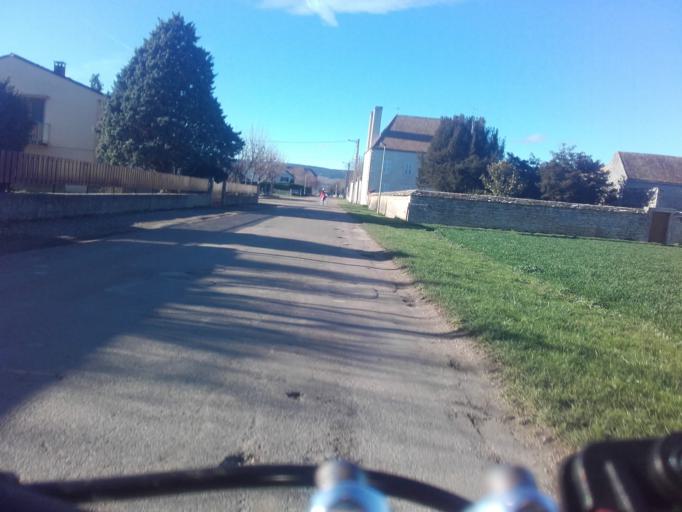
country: FR
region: Bourgogne
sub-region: Departement de la Cote-d'Or
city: Corpeau
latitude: 46.9277
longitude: 4.7861
